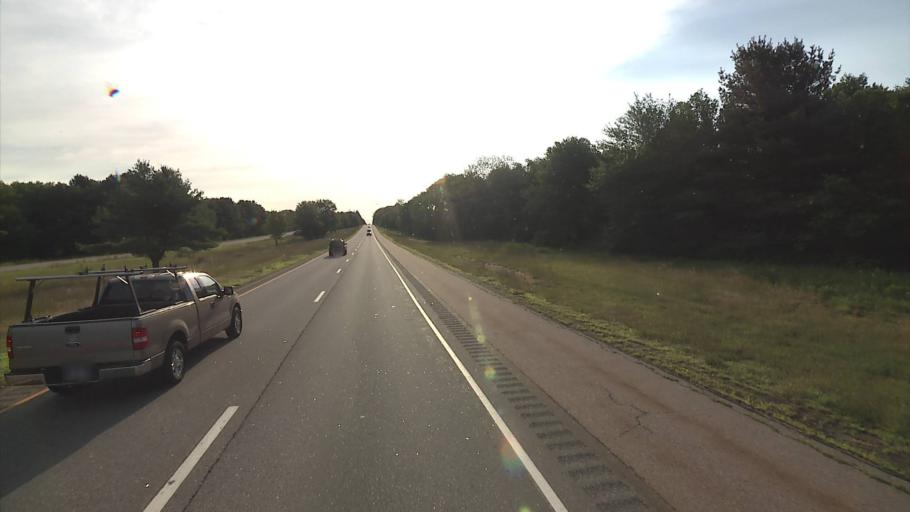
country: US
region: Connecticut
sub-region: New London County
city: Colchester
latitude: 41.5656
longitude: -72.2379
